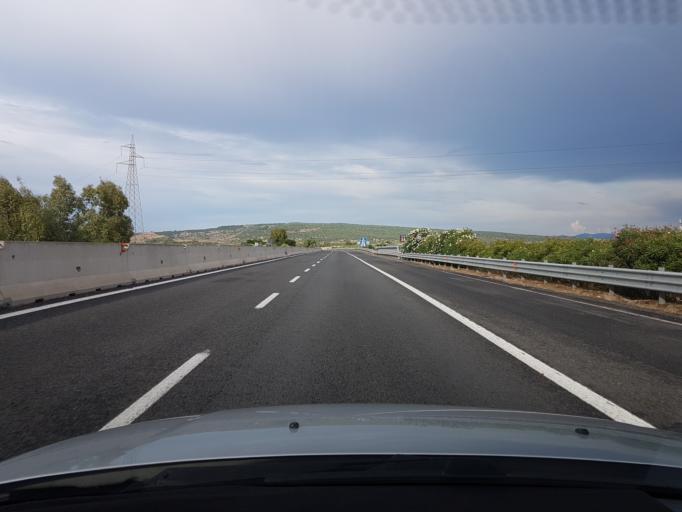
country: IT
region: Sardinia
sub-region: Provincia di Oristano
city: Tramatza
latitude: 39.9952
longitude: 8.6515
